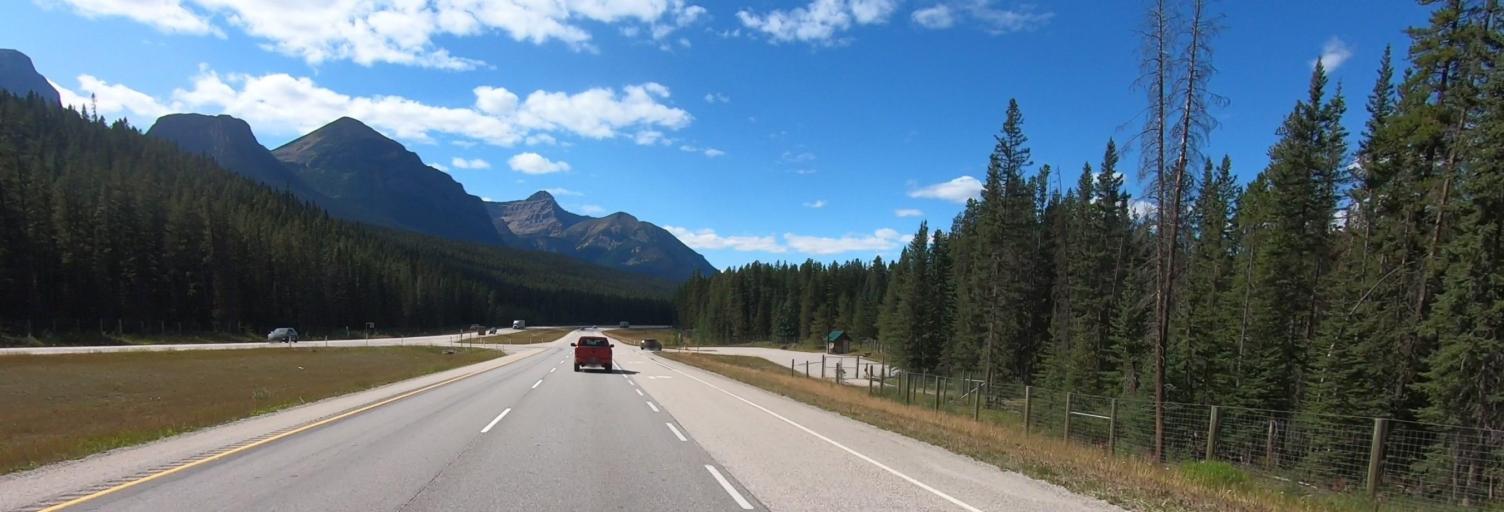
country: CA
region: Alberta
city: Lake Louise
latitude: 51.3961
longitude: -116.1455
